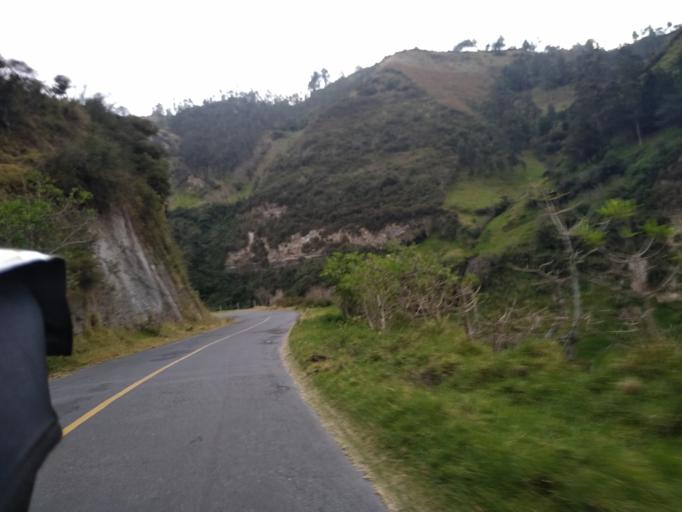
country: EC
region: Cotopaxi
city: Saquisili
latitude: -0.6914
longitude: -78.8701
